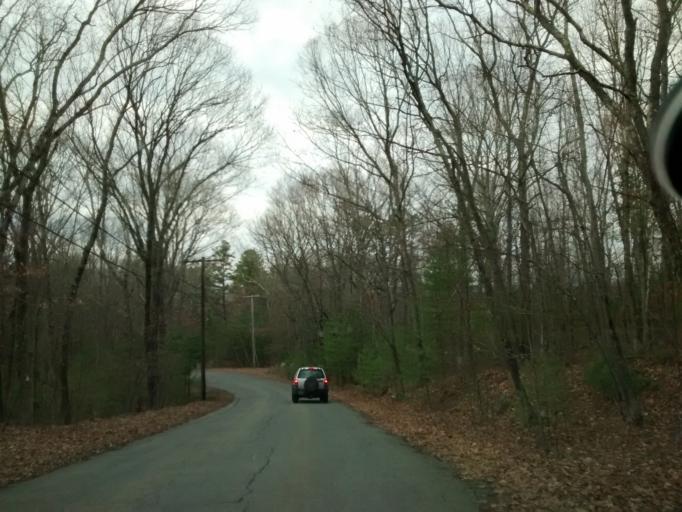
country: US
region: Massachusetts
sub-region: Worcester County
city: Millville
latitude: 42.0249
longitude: -71.5997
